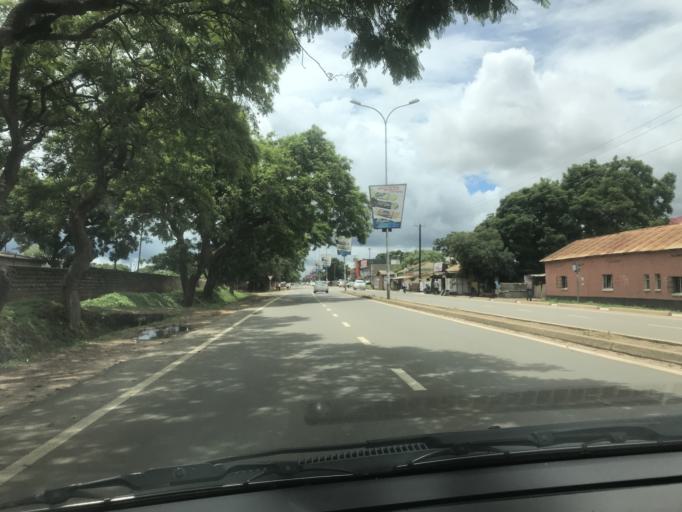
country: ZM
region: Lusaka
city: Lusaka
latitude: -15.4322
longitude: 28.3057
